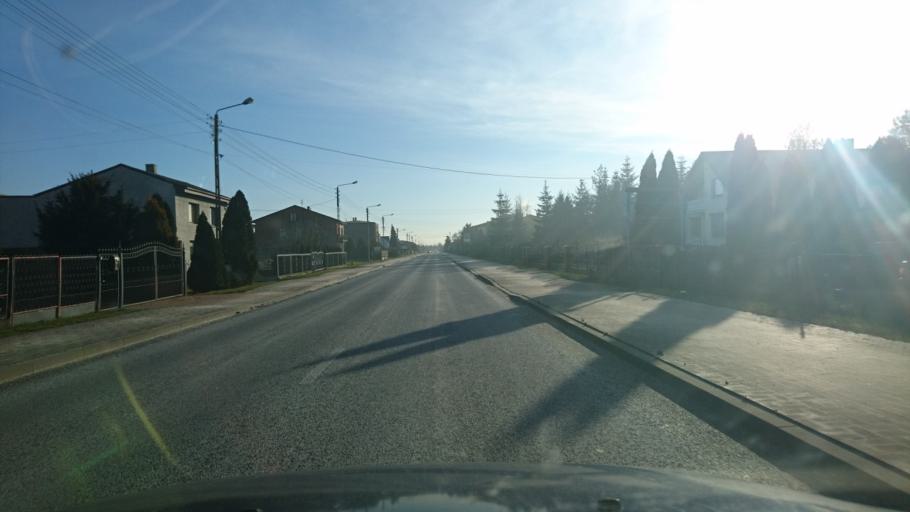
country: PL
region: Silesian Voivodeship
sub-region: Powiat klobucki
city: Starokrzepice
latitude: 51.0132
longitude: 18.6553
